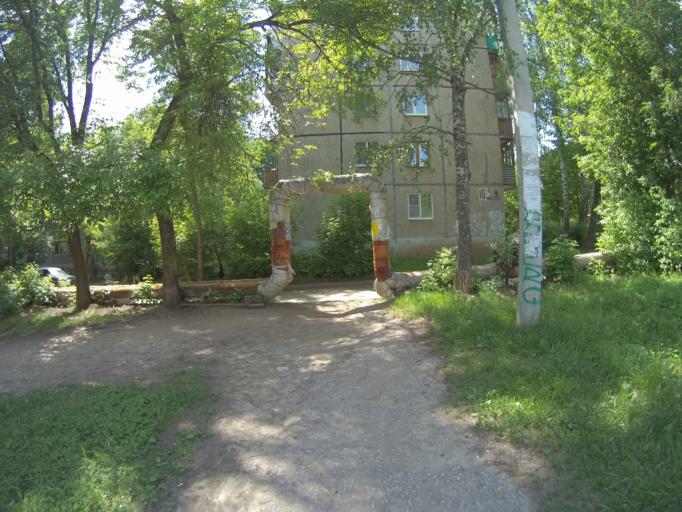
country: RU
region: Vladimir
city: Vladimir
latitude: 56.1267
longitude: 40.3513
